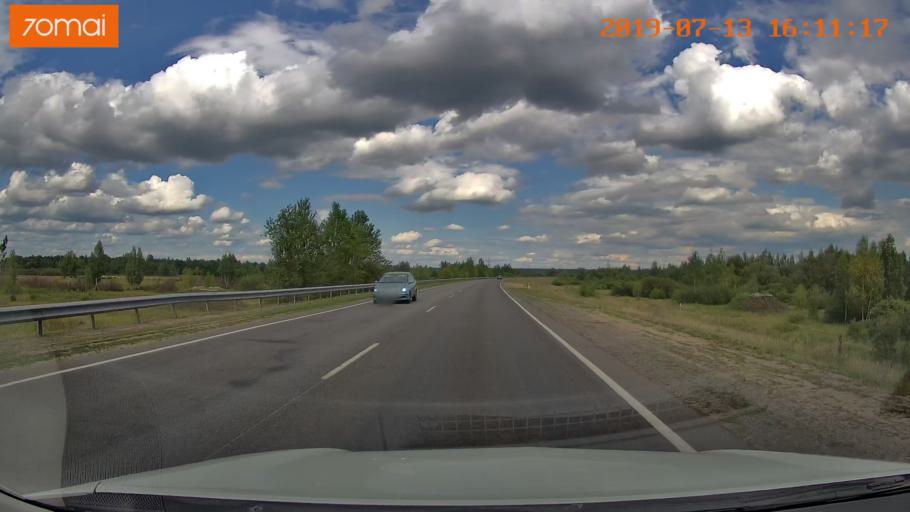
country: BY
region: Mogilev
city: Babruysk
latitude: 53.1661
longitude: 29.2534
